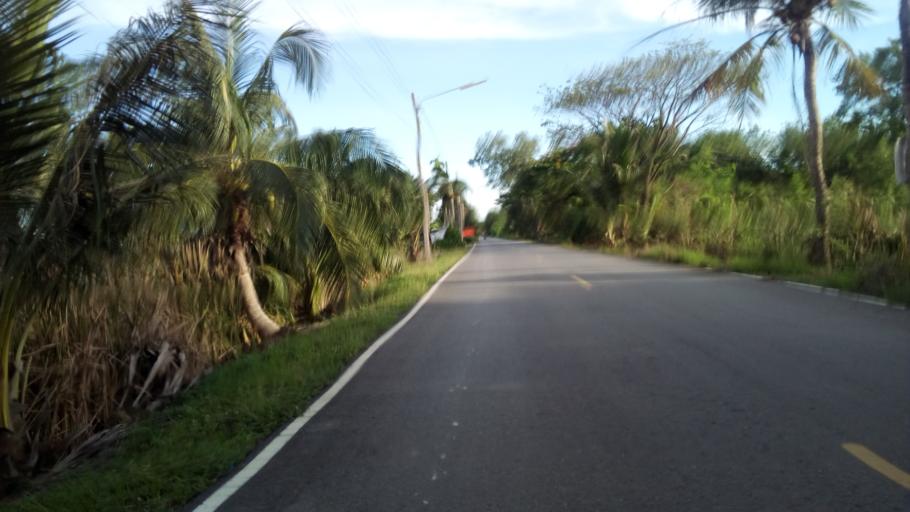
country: TH
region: Pathum Thani
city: Ban Lam Luk Ka
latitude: 14.0159
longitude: 100.8462
